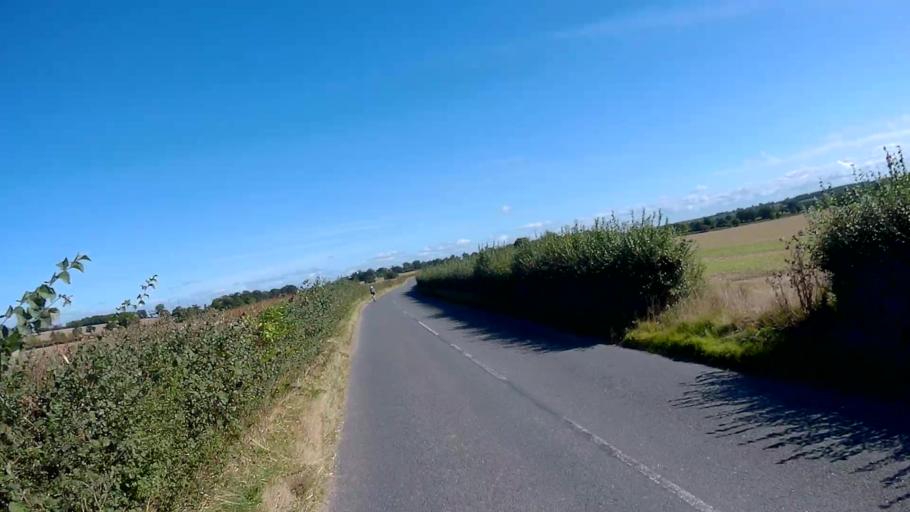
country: GB
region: England
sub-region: West Berkshire
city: Stratfield Mortimer
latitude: 51.3678
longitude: -1.0170
